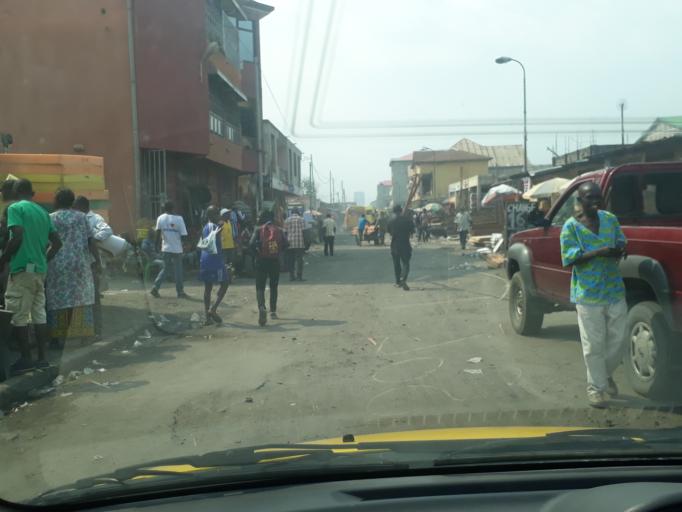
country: CD
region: Kinshasa
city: Kinshasa
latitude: -4.3258
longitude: 15.3171
